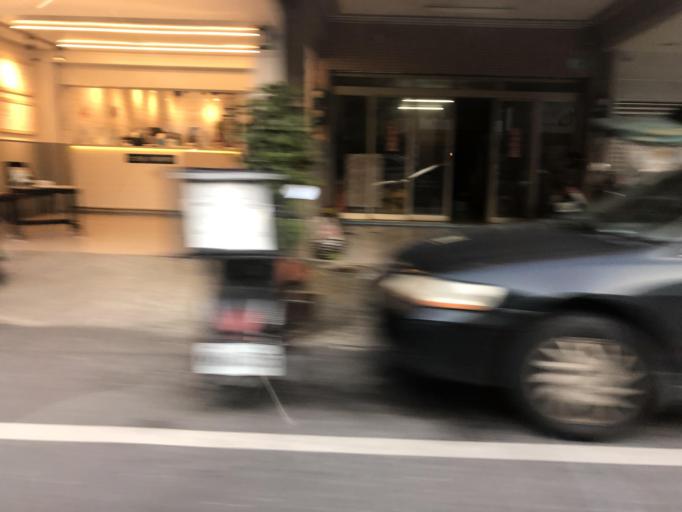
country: TW
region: Taiwan
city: Xinying
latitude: 23.1822
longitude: 120.2515
